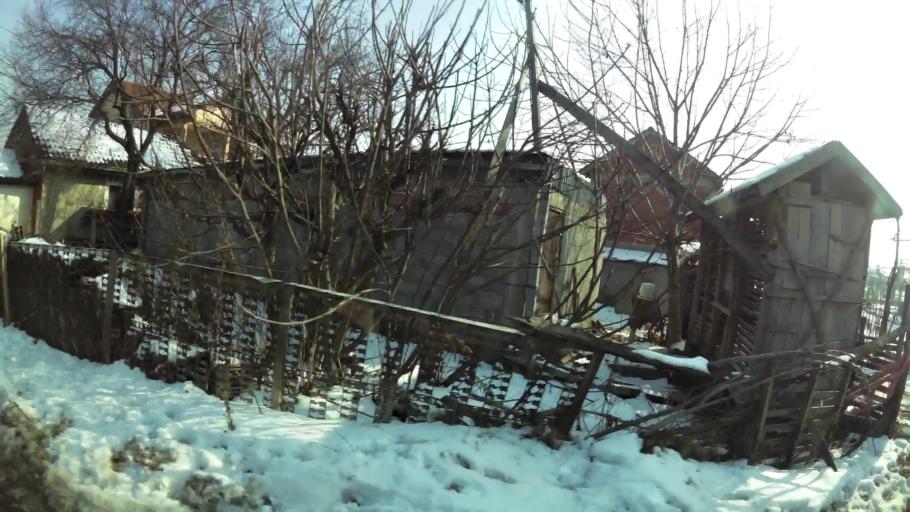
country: MK
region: Suto Orizari
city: Suto Orizare
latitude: 42.0265
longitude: 21.3807
